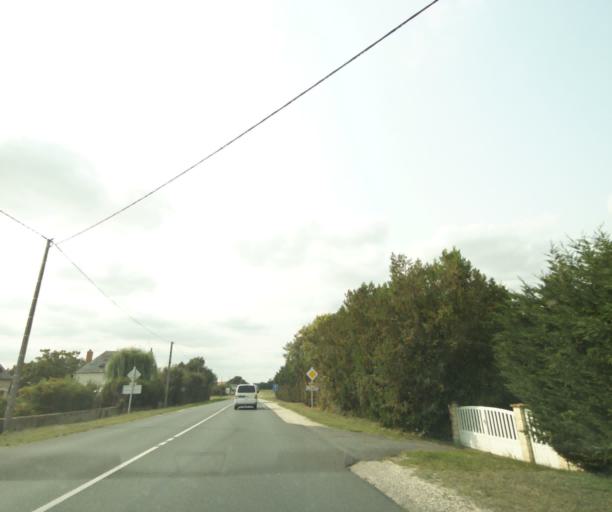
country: FR
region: Centre
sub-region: Departement de l'Indre
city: Chatillon-sur-Indre
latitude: 46.9970
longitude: 1.1564
